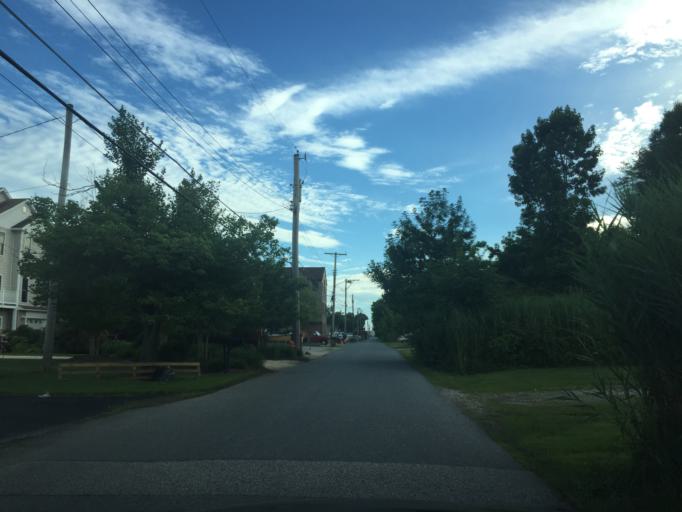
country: US
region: Maryland
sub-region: Baltimore County
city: Bowleys Quarters
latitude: 39.3029
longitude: -76.3742
